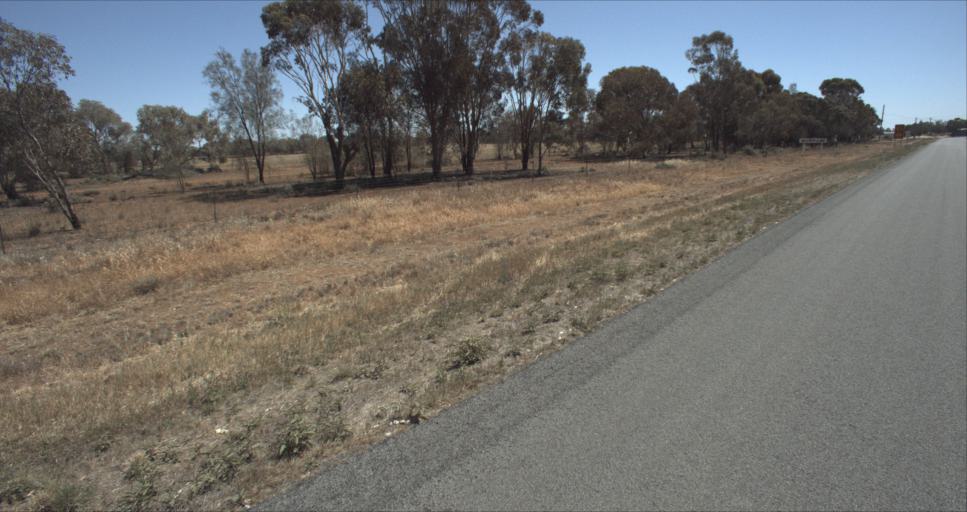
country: AU
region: New South Wales
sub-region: Leeton
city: Leeton
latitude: -34.4303
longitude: 146.2997
